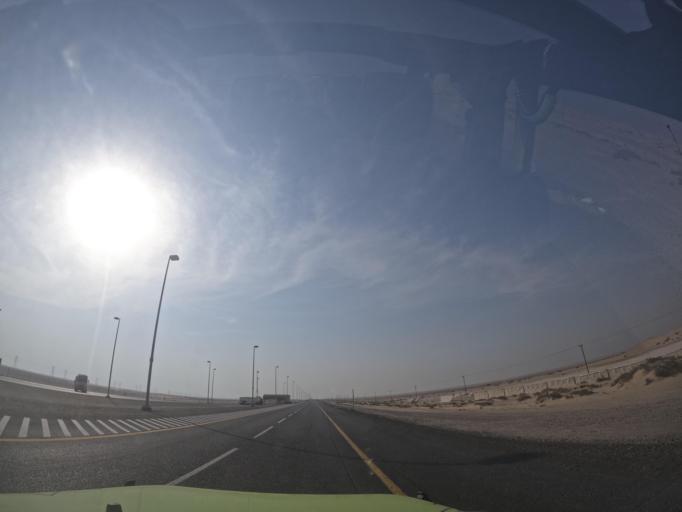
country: AE
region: Dubai
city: Dubai
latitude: 24.7667
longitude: 55.0940
